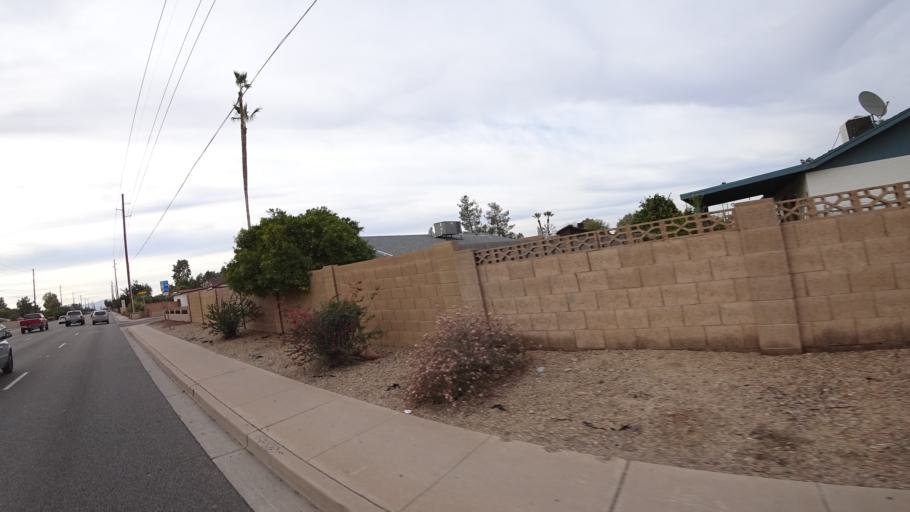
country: US
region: Arizona
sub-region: Maricopa County
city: Glendale
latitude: 33.5676
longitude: -112.1780
